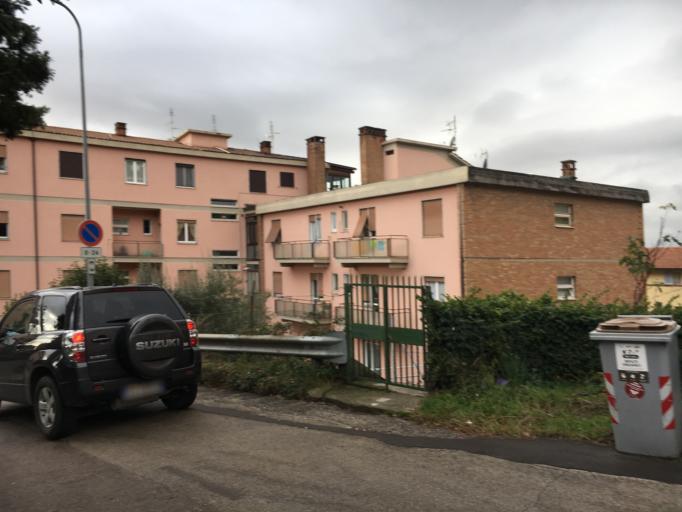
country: IT
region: Umbria
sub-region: Provincia di Perugia
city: Perugia
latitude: 43.1175
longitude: 12.3774
